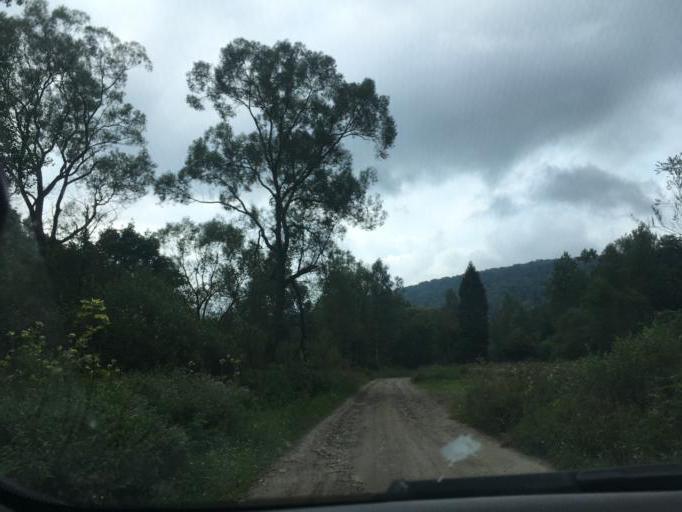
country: PL
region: Subcarpathian Voivodeship
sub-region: Powiat bieszczadzki
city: Lutowiska
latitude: 49.1749
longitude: 22.6135
